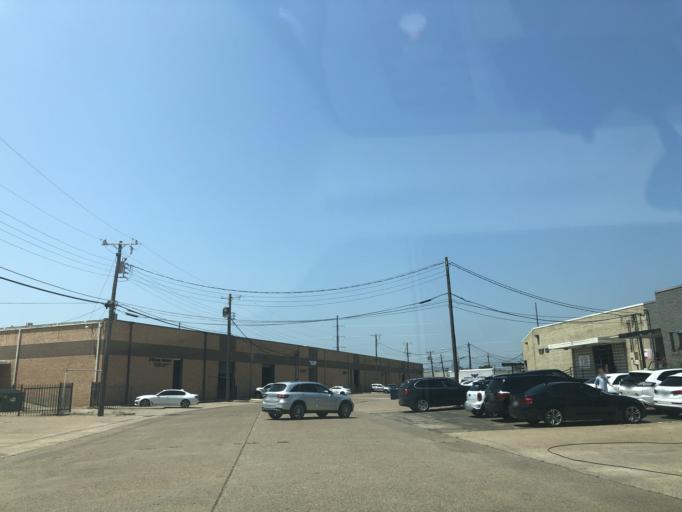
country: US
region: Texas
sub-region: Dallas County
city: Dallas
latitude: 32.8026
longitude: -96.8391
